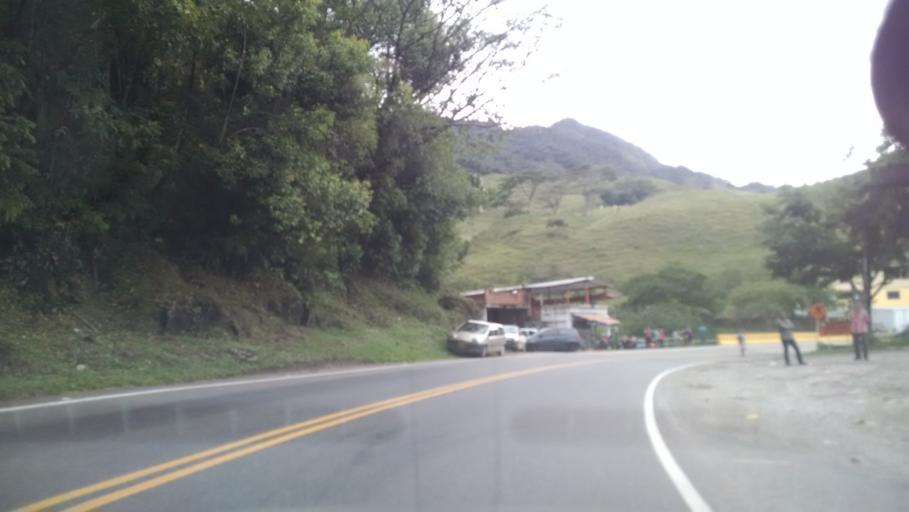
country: CO
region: Antioquia
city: Cocorna
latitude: 6.0249
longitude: -75.1699
